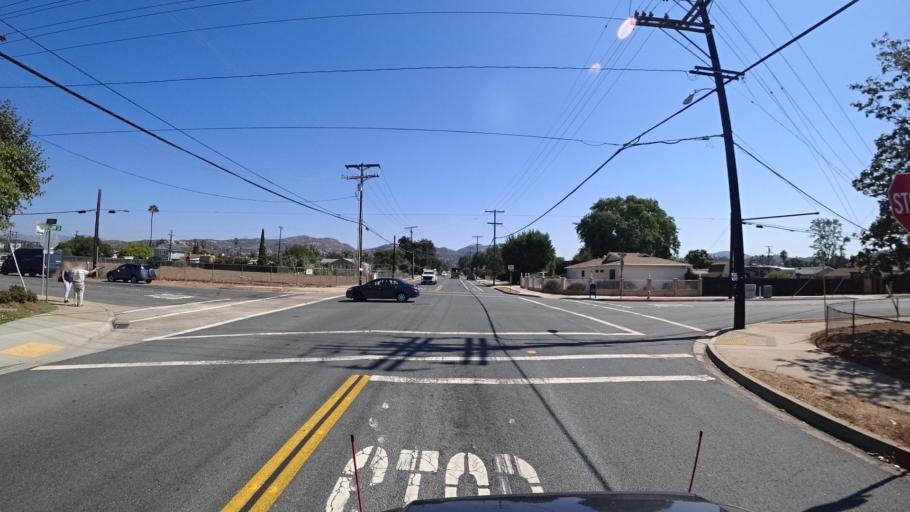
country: US
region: California
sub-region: San Diego County
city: Bostonia
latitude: 32.8002
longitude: -116.9272
